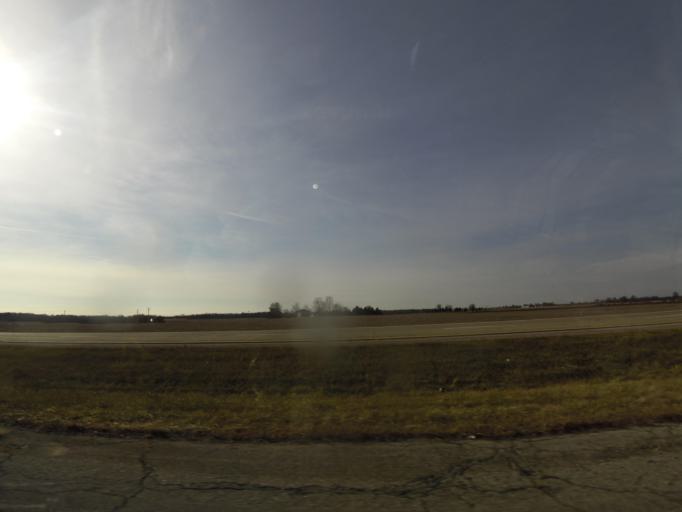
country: US
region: Illinois
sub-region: De Witt County
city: Clinton
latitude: 40.1415
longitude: -88.9806
